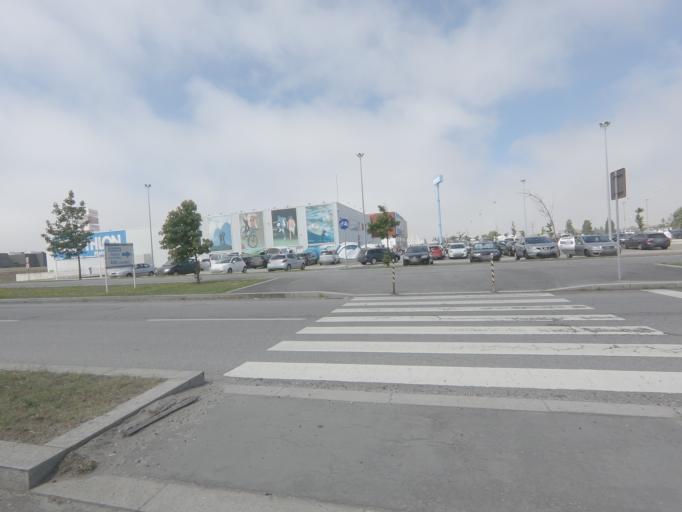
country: PT
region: Porto
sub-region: Matosinhos
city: Santa Cruz do Bispo
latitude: 41.2164
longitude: -8.6835
